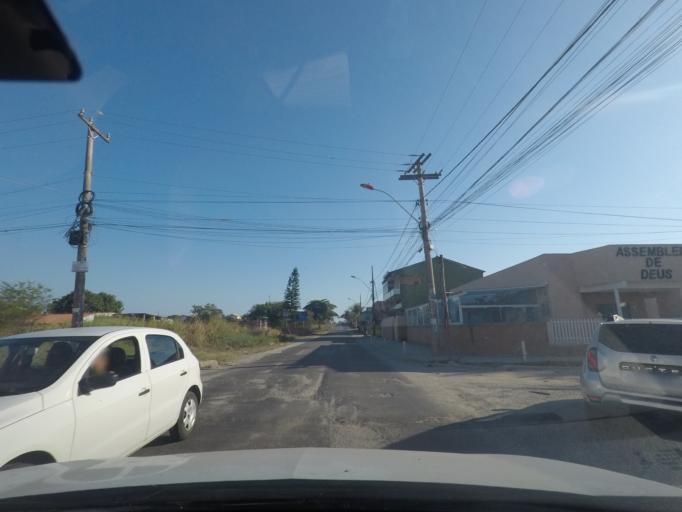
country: BR
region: Rio de Janeiro
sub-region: Marica
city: Marica
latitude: -22.9644
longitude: -42.9424
